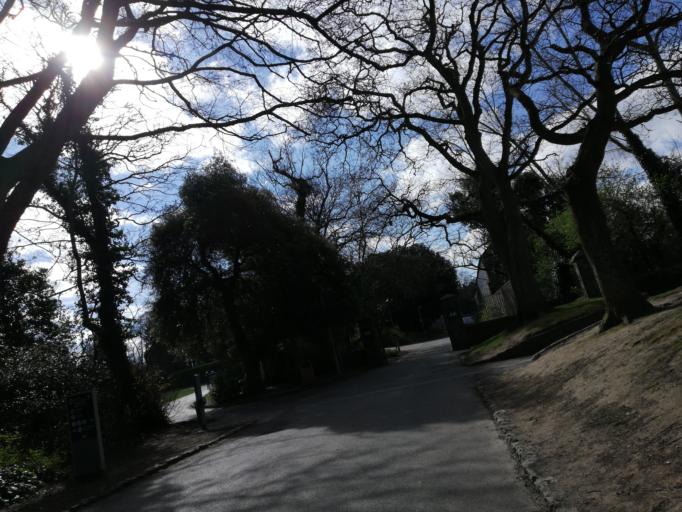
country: IE
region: Leinster
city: Malahide
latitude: 53.4473
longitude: -6.1588
